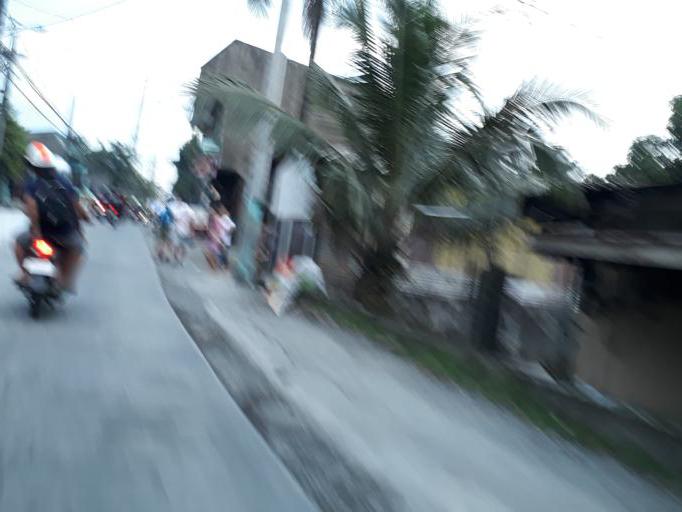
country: PH
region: Central Luzon
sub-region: Province of Bulacan
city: Meycauayan
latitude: 14.7254
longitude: 120.9877
